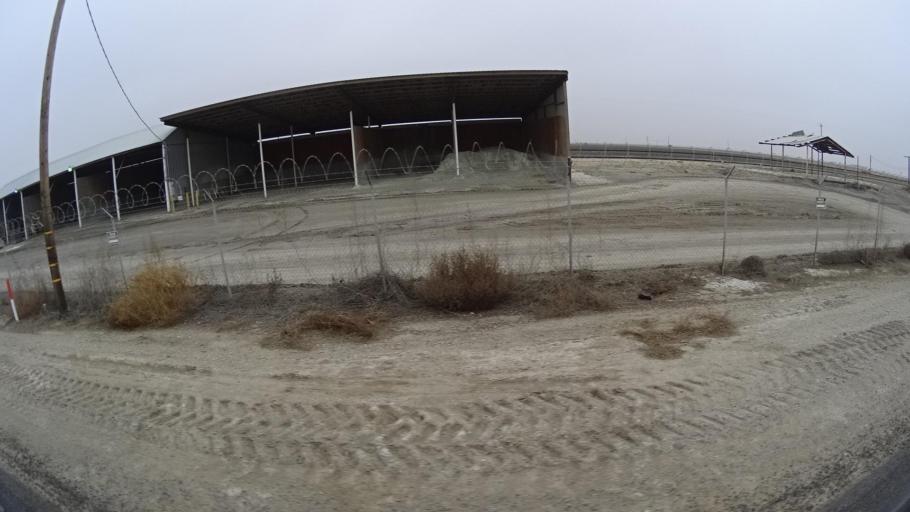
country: US
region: California
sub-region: Kern County
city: Rosedale
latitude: 35.1804
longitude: -119.1969
